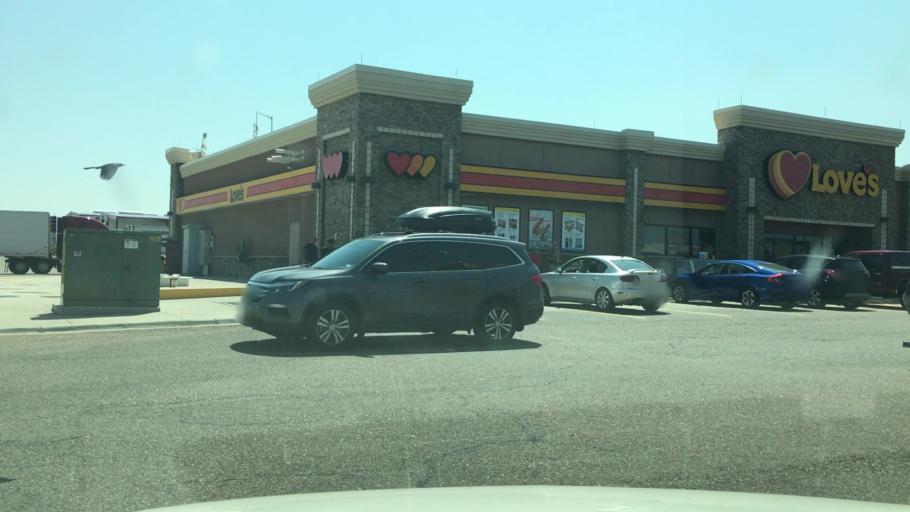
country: US
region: New Mexico
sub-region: Quay County
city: Tucumcari
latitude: 35.1592
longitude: -103.7016
